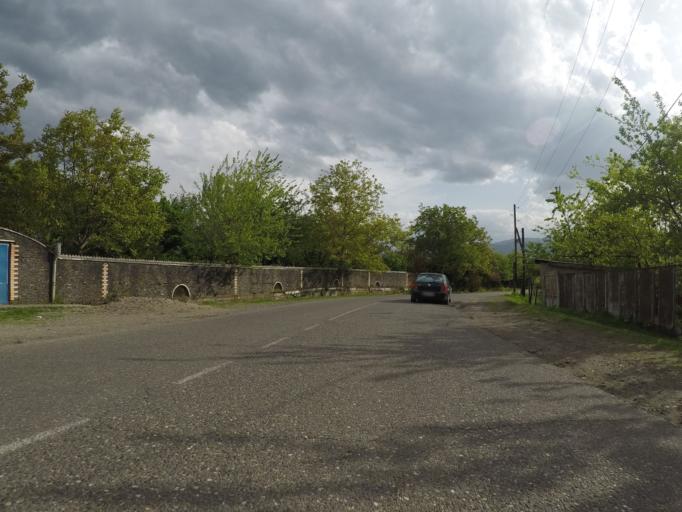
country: GE
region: Imereti
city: Zestap'oni
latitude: 42.1207
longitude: 43.0620
